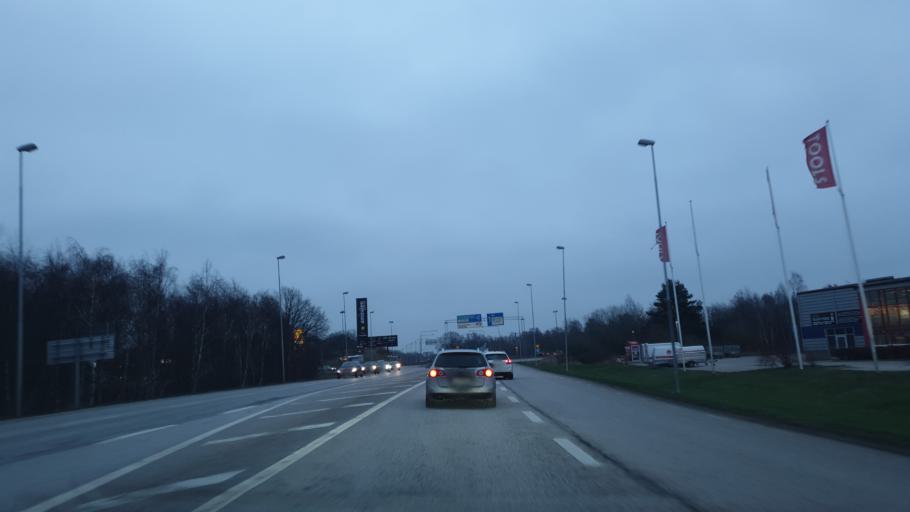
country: SE
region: Blekinge
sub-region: Karlskrona Kommun
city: Karlskrona
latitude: 56.1960
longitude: 15.6358
